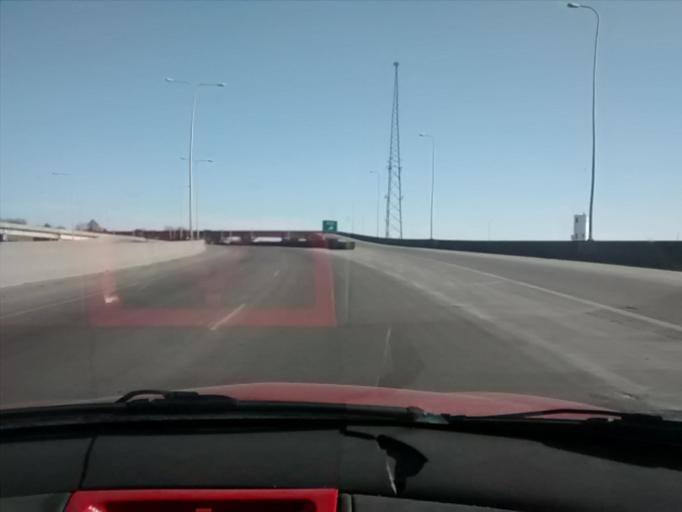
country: US
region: Nebraska
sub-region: Douglas County
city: Omaha
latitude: 41.2282
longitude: -95.9552
